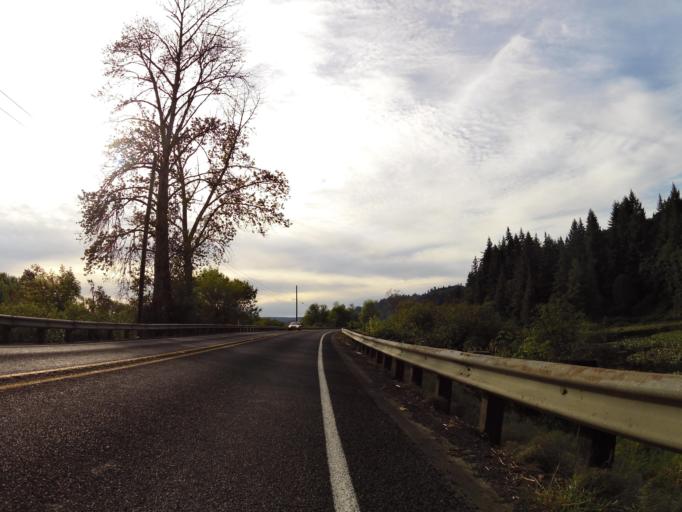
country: US
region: Washington
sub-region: Cowlitz County
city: West Longview
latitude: 46.1831
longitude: -123.0743
